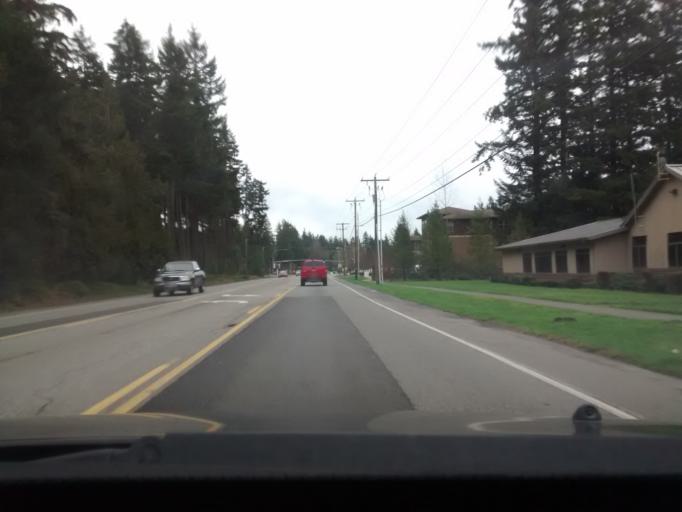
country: US
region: Washington
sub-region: Kitsap County
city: East Port Orchard
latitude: 47.5194
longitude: -122.6135
